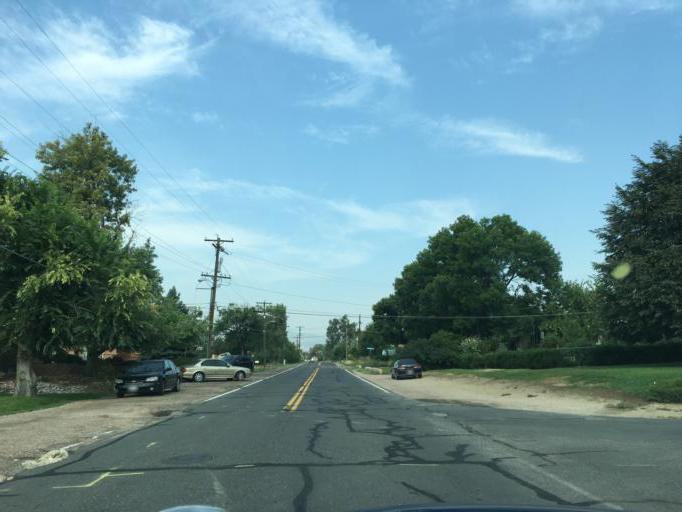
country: US
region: Colorado
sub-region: Jefferson County
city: Arvada
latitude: 39.8096
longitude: -105.0859
